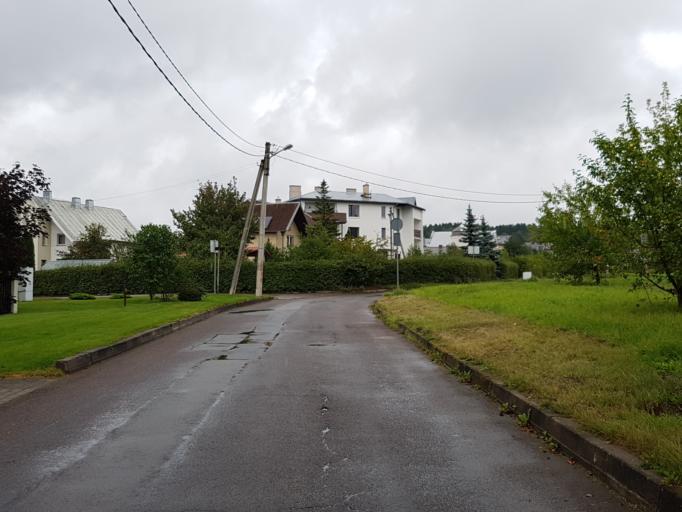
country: LT
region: Vilnius County
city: Lazdynai
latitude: 54.6625
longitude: 25.1855
